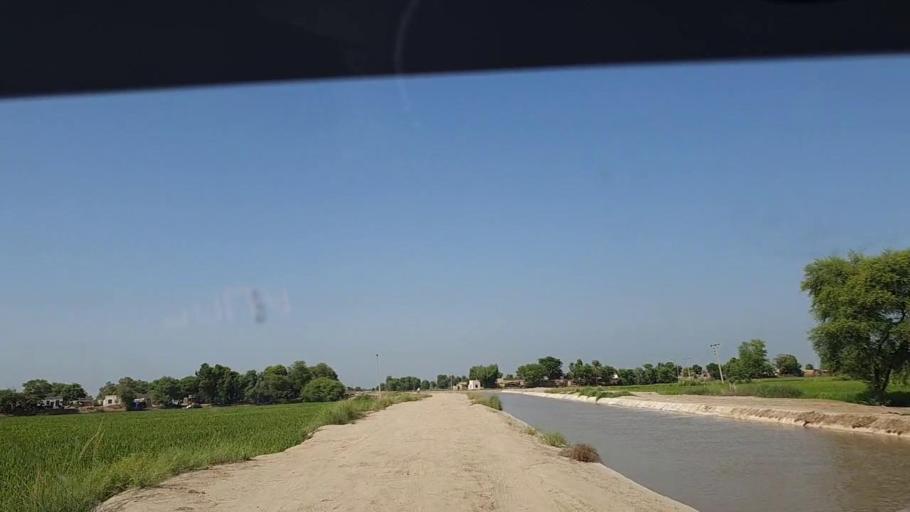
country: PK
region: Sindh
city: Ghauspur
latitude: 28.1727
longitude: 69.0988
